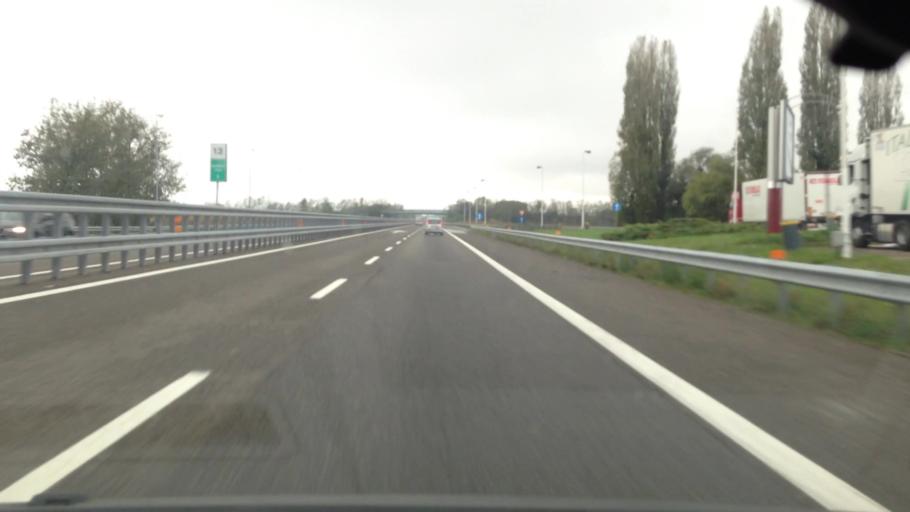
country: IT
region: Piedmont
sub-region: Provincia di Asti
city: Villanova d'Asti
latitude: 44.9501
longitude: 7.9505
